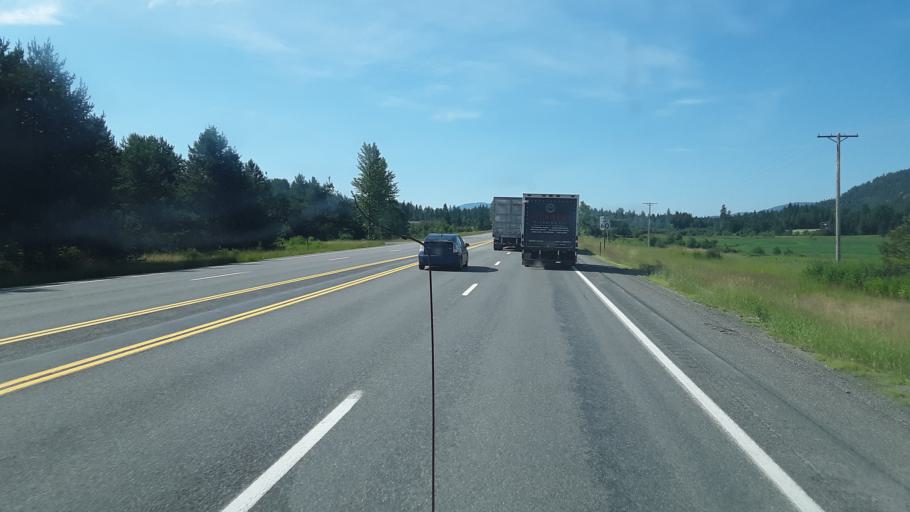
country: US
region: Idaho
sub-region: Bonner County
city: Ponderay
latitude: 48.3560
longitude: -116.5475
